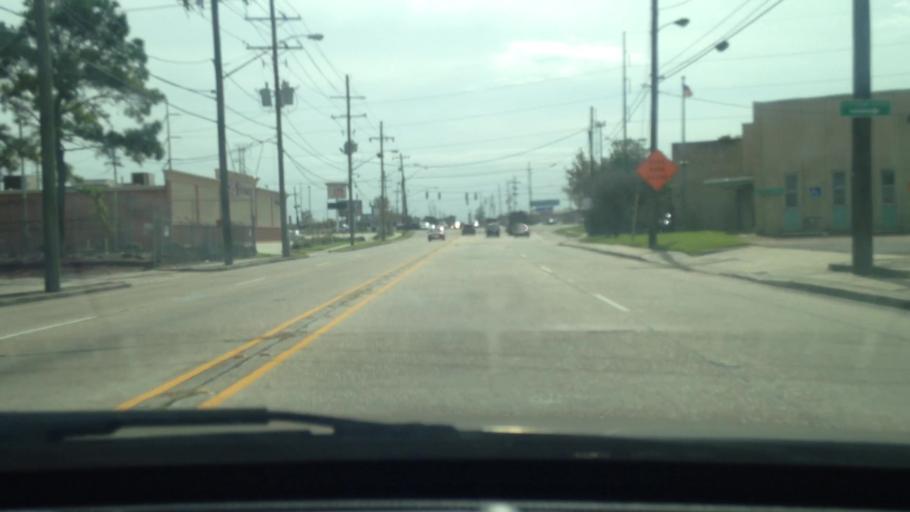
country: US
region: Louisiana
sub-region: Jefferson Parish
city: River Ridge
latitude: 29.9793
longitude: -90.2115
